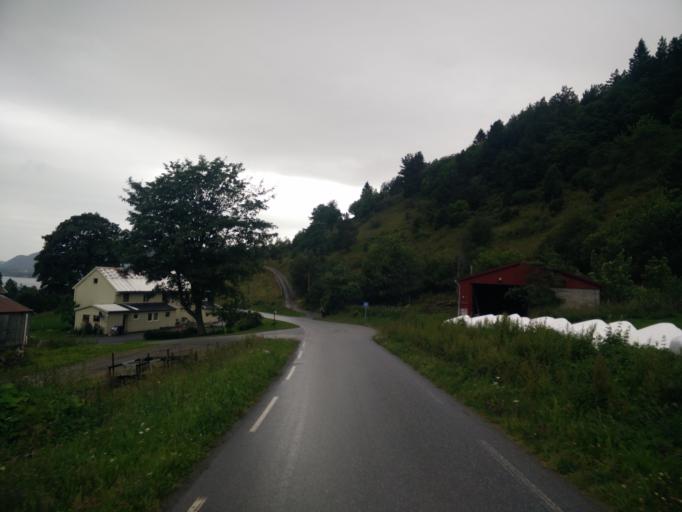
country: NO
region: More og Romsdal
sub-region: Kristiansund
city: Rensvik
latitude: 63.0156
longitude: 7.9104
